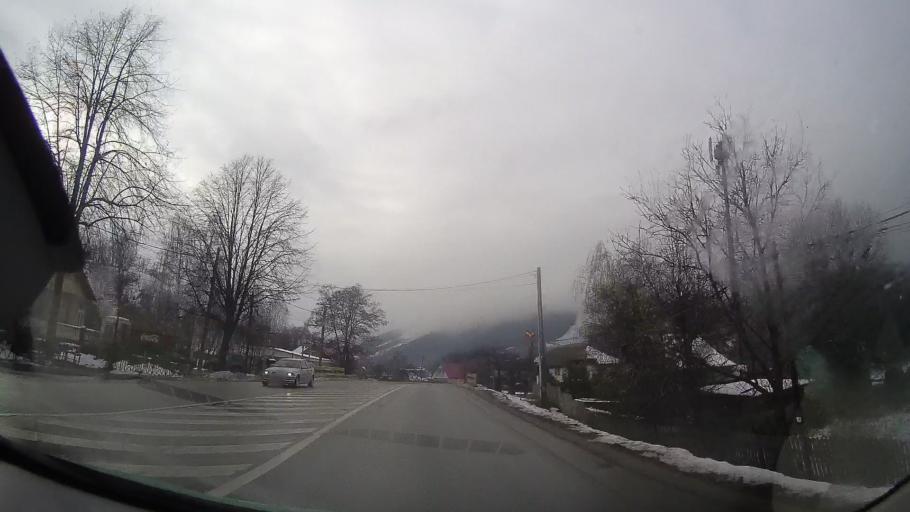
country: RO
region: Neamt
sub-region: Comuna Tasca
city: Tasca
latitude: 46.8939
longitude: 26.0222
